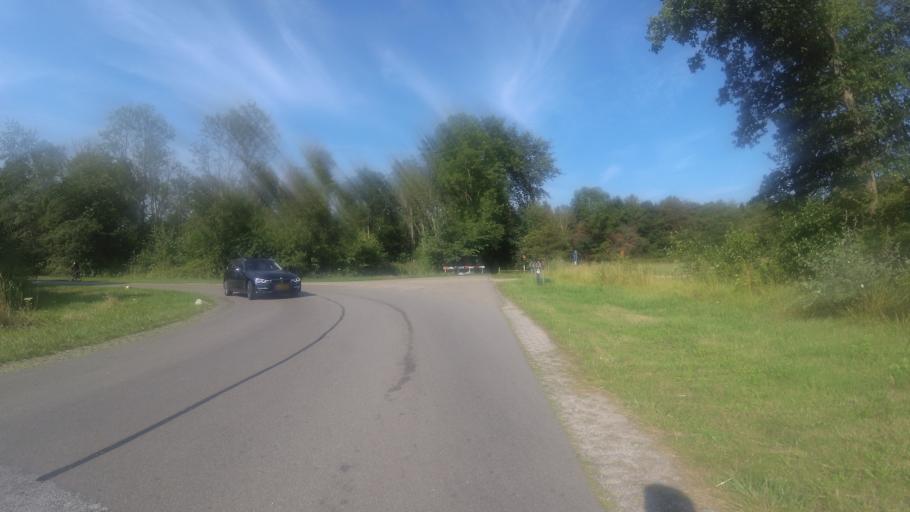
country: NL
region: Zeeland
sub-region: Gemeente Veere
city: Veere
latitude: 51.5856
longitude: 3.6592
